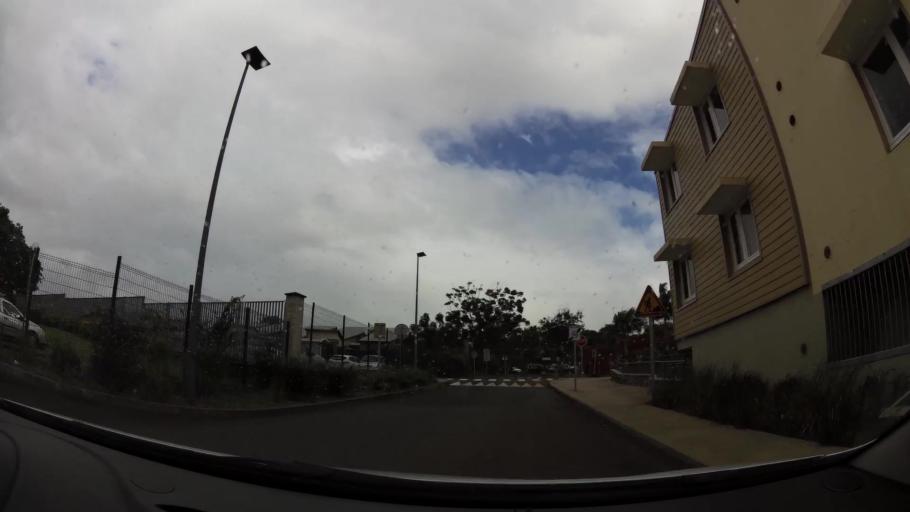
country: RE
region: Reunion
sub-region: Reunion
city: Sainte-Suzanne
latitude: -20.9023
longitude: 55.5978
